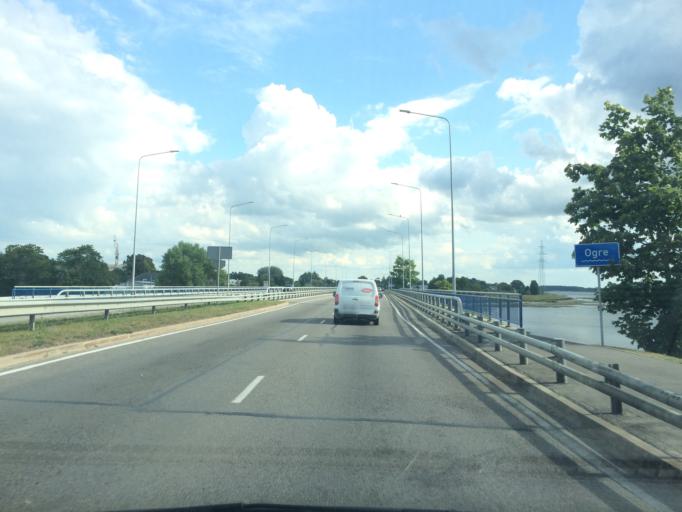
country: LV
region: Ogre
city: Ogre
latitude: 56.8115
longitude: 24.5995
